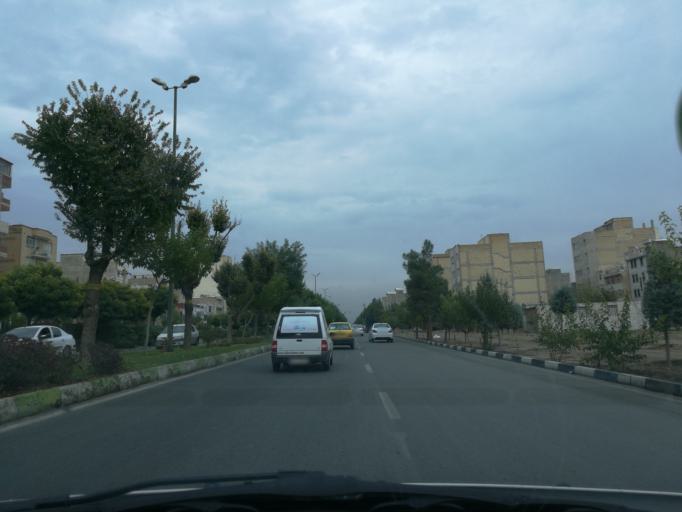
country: IR
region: Alborz
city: Karaj
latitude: 35.8609
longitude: 50.9395
